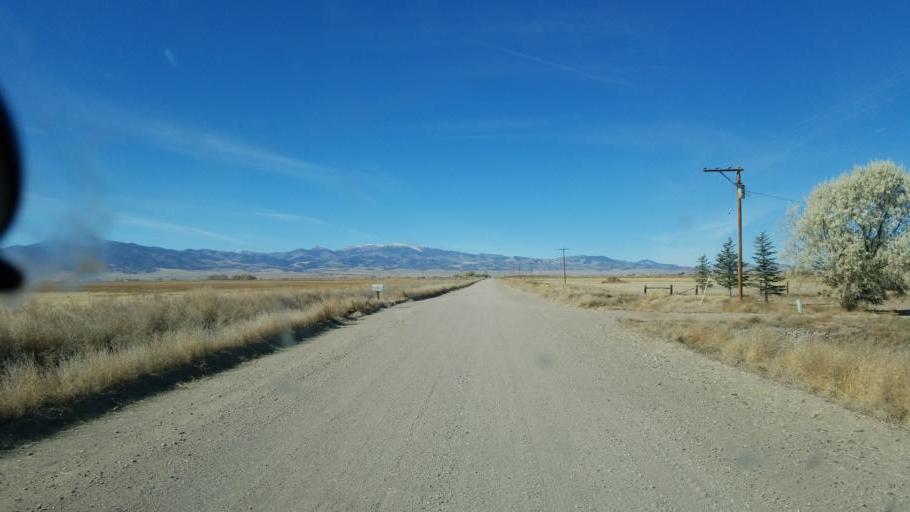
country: US
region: Colorado
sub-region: Rio Grande County
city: Monte Vista
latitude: 37.5315
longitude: -106.0659
